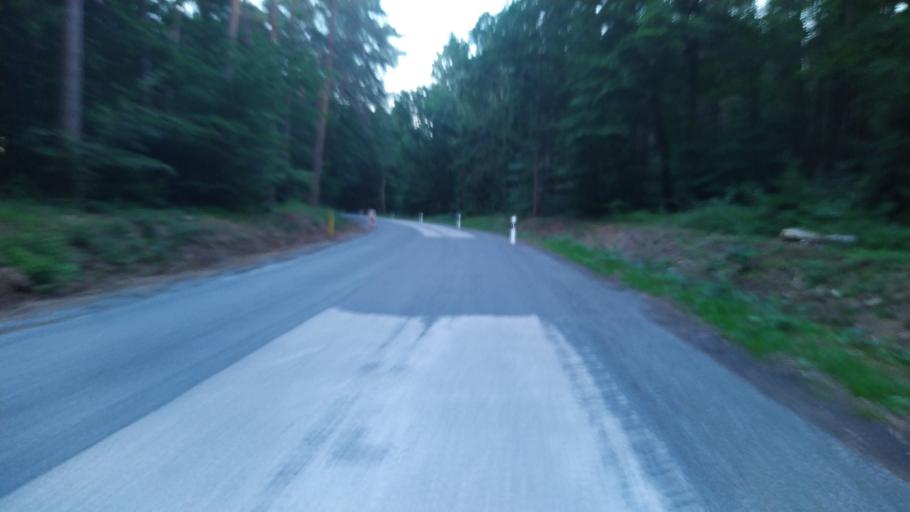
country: DE
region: Lower Saxony
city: Deinstedt
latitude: 53.4906
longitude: 9.2282
